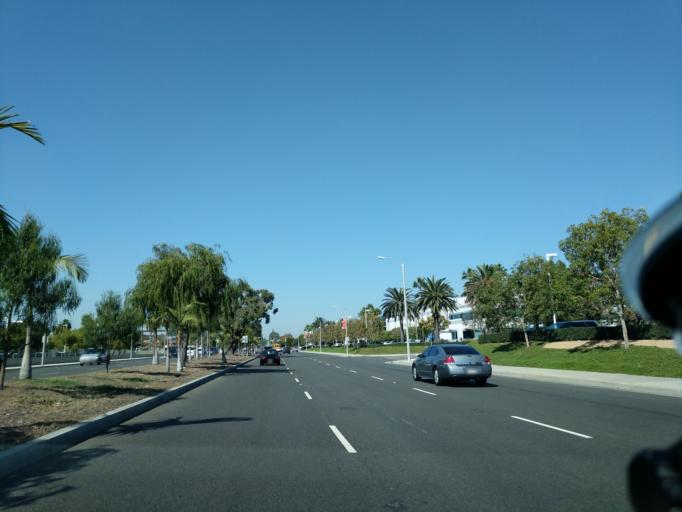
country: US
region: California
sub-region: Orange County
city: Cypress
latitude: 33.8006
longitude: -118.0283
